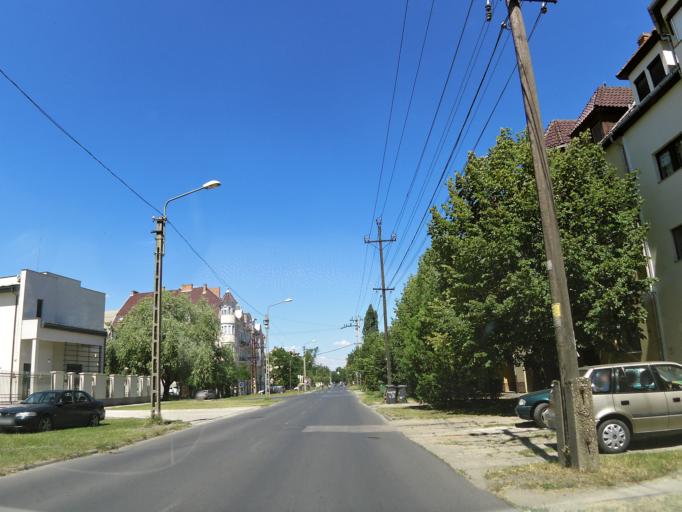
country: HU
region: Csongrad
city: Szeged
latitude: 46.2639
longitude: 20.1362
